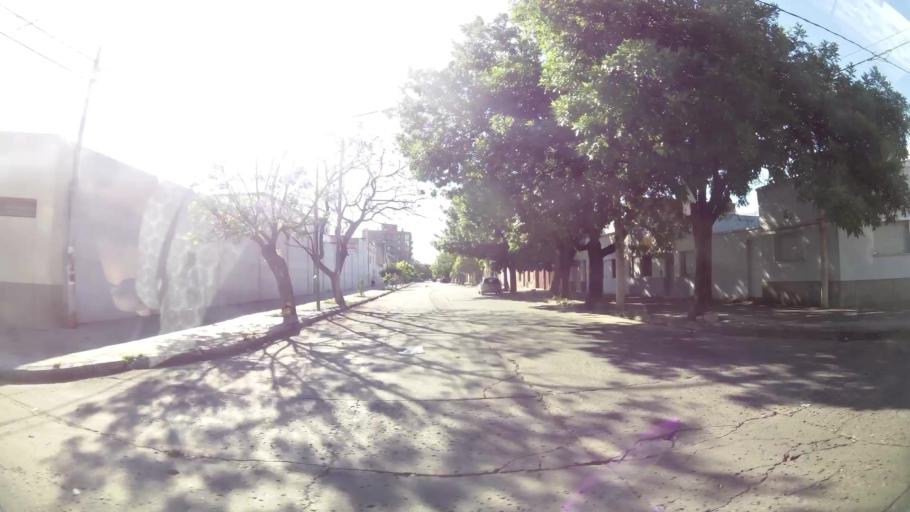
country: AR
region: Cordoba
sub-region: Departamento de Capital
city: Cordoba
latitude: -31.3945
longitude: -64.1739
